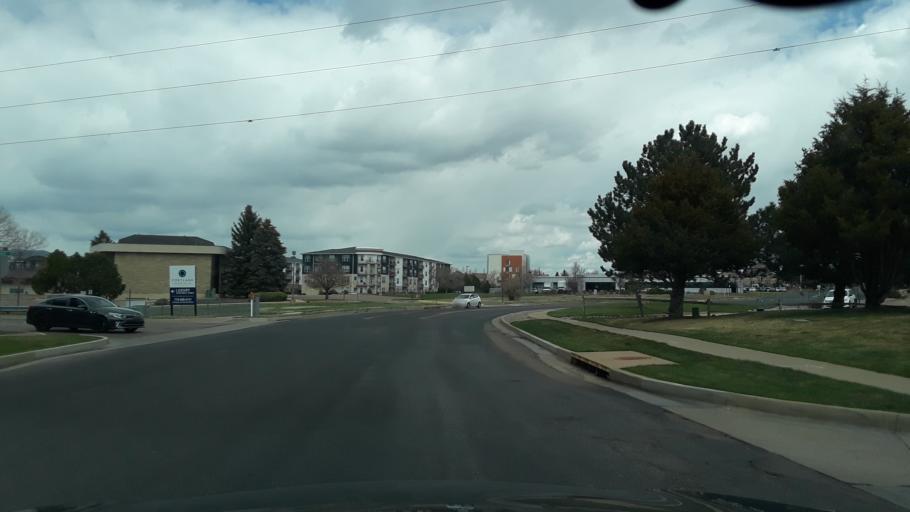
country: US
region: Colorado
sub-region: El Paso County
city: Air Force Academy
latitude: 38.9438
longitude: -104.8040
